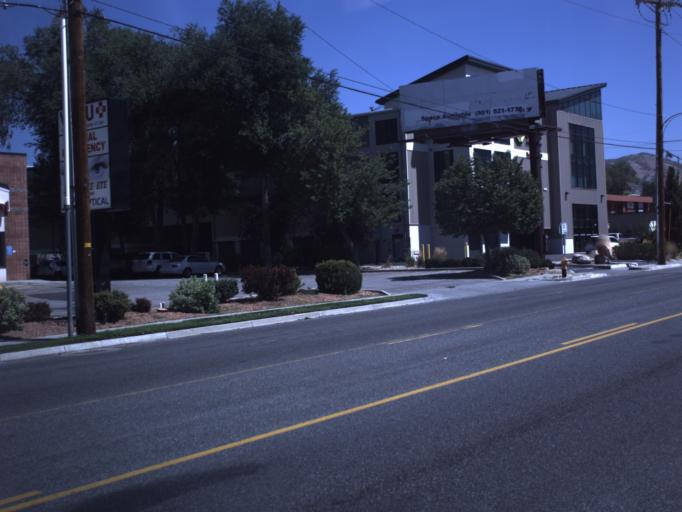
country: US
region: Utah
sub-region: Salt Lake County
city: Millcreek
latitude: 40.6998
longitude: -111.8622
